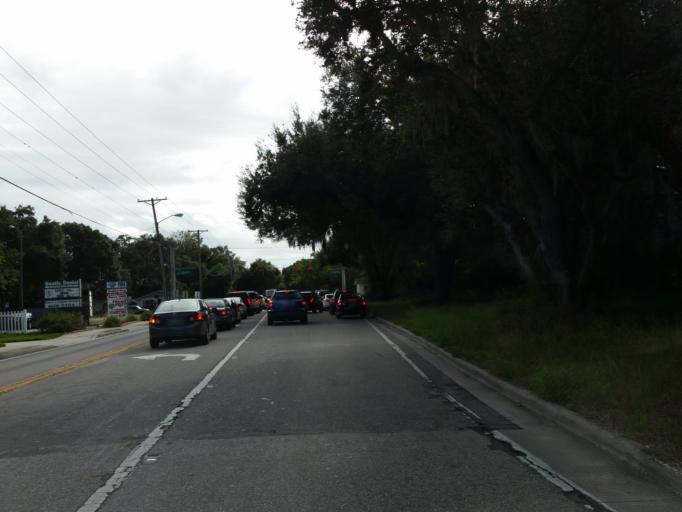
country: US
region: Florida
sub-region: Hillsborough County
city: Brandon
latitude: 27.9244
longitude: -82.2858
